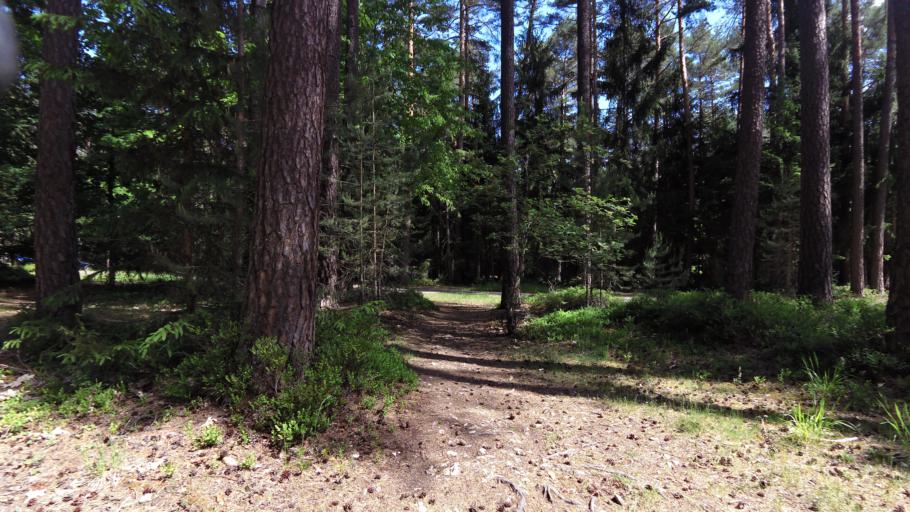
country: DE
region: Bavaria
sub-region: Regierungsbezirk Mittelfranken
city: Pleinfeld
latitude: 49.1180
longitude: 10.9631
